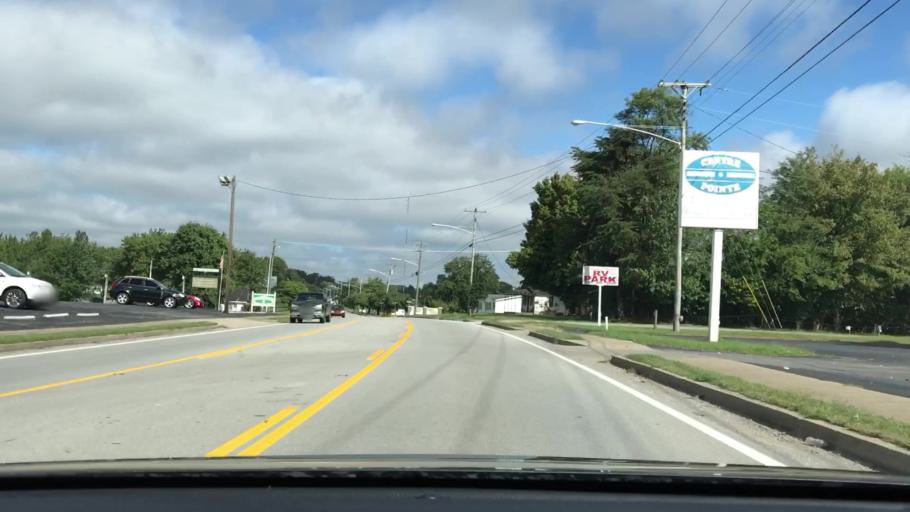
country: US
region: Kentucky
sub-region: Russell County
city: Russell Springs
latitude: 37.0213
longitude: -85.0761
